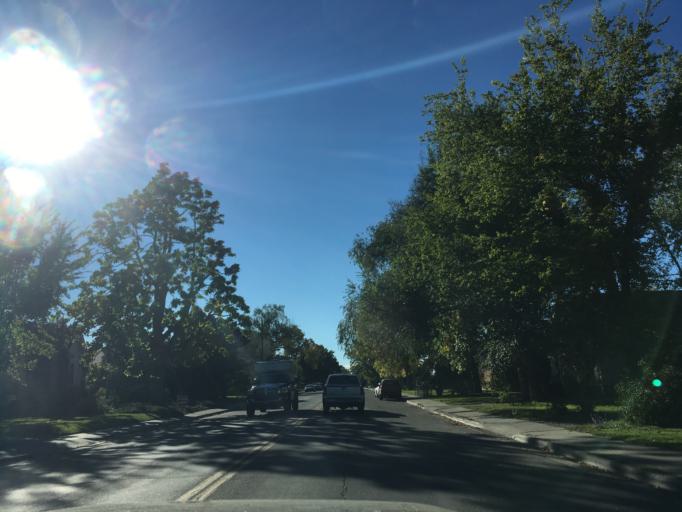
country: US
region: Montana
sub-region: Yellowstone County
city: Billings
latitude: 45.7899
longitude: -108.5320
